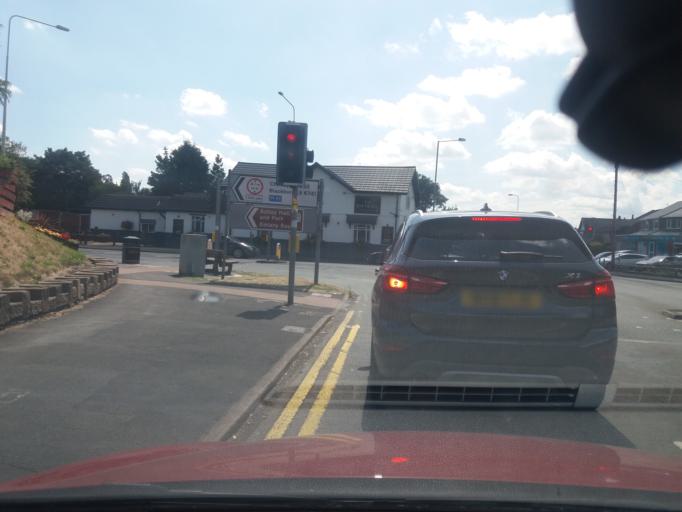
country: GB
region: England
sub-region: Lancashire
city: Euxton
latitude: 53.6707
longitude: -2.6763
